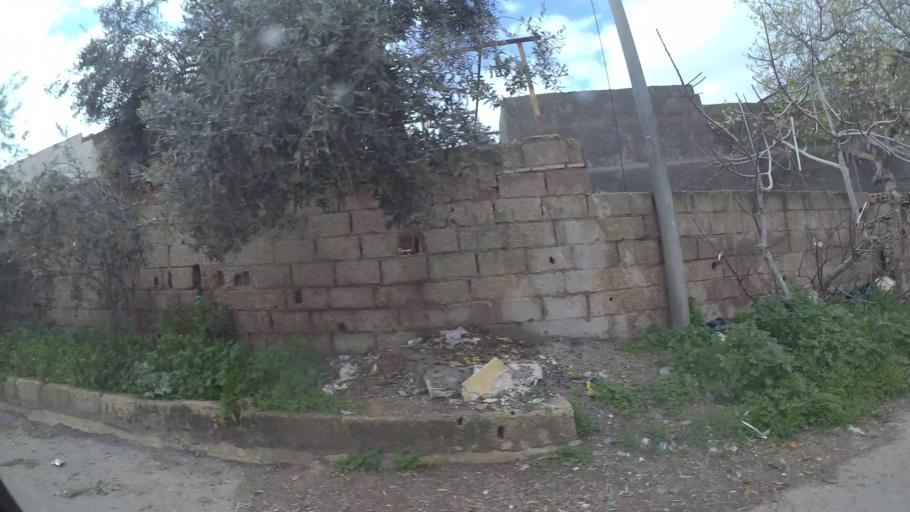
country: JO
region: Amman
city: Al Jubayhah
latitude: 32.0539
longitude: 35.8321
